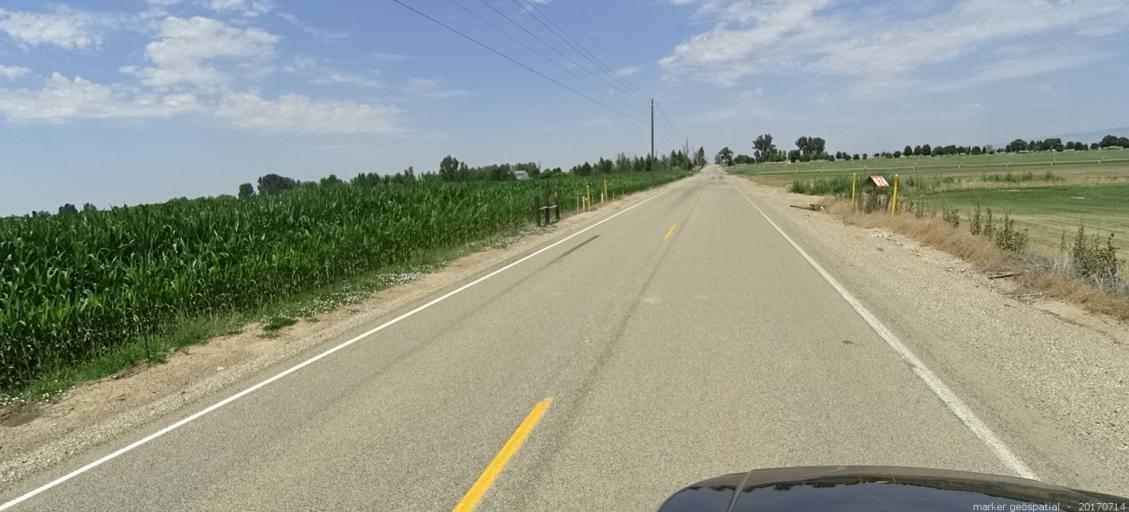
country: US
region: Idaho
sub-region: Ada County
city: Kuna
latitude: 43.5350
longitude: -116.3543
